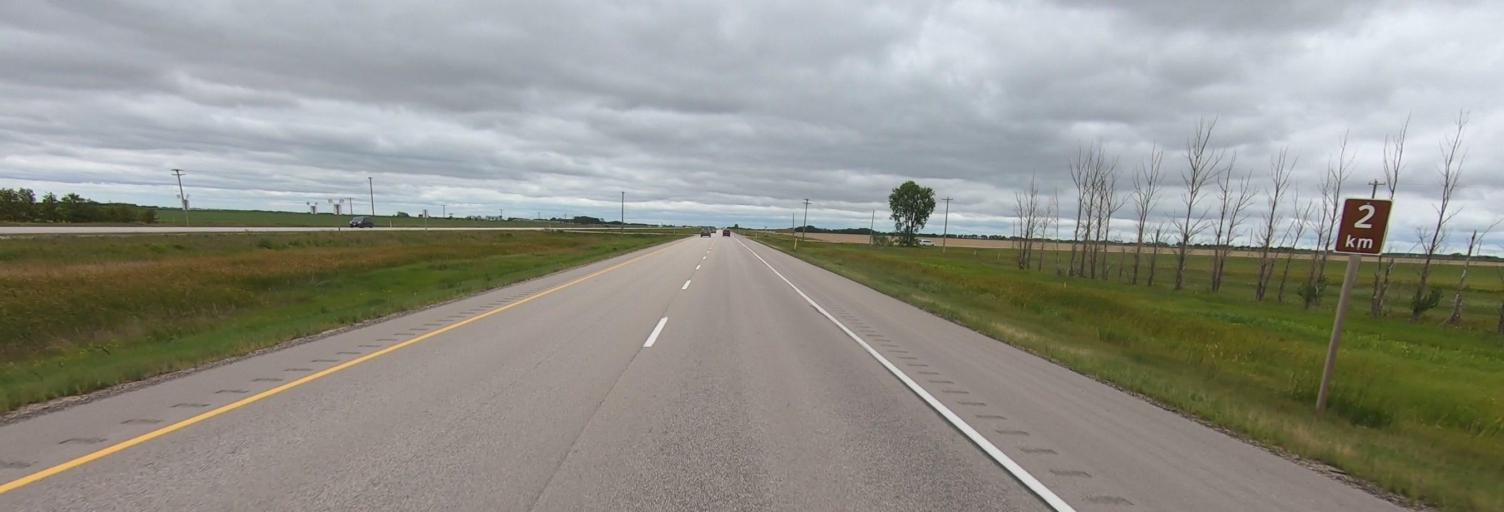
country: CA
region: Manitoba
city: Headingley
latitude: 49.9151
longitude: -97.8006
